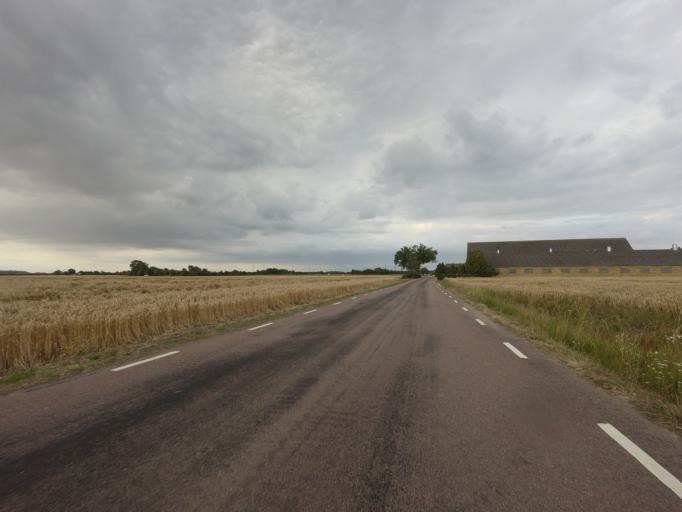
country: SE
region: Skane
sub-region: Helsingborg
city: Odakra
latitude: 56.1433
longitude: 12.7313
